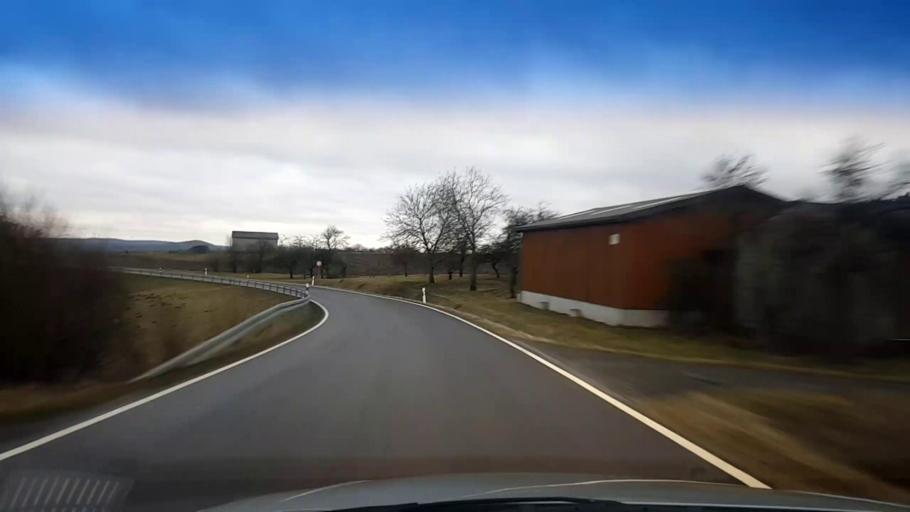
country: DE
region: Bavaria
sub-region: Upper Franconia
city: Wattendorf
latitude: 50.0292
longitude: 11.0653
